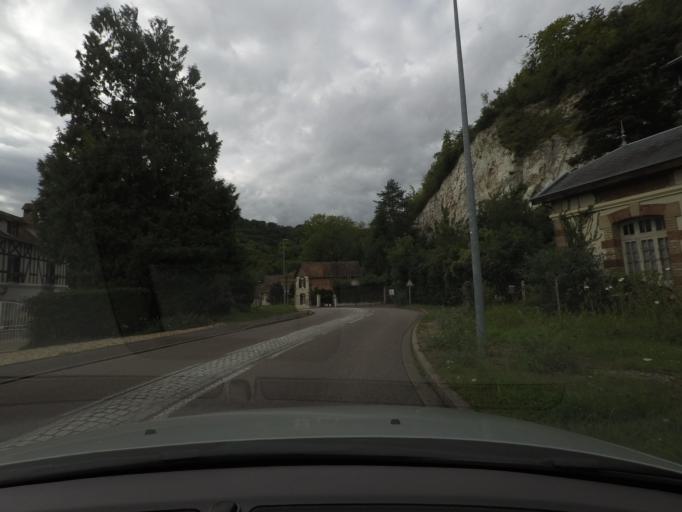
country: FR
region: Haute-Normandie
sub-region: Departement de l'Eure
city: Les Andelys
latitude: 49.2525
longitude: 1.3812
